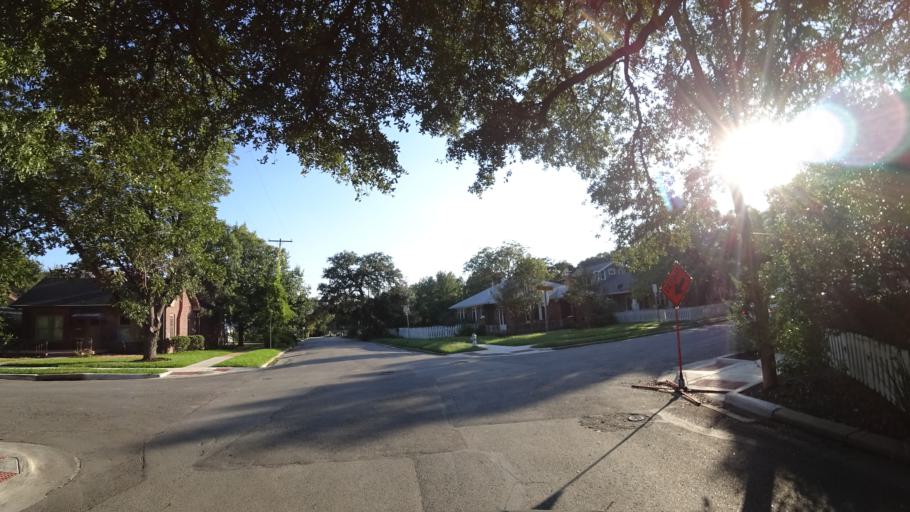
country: US
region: Texas
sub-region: Travis County
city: Austin
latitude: 30.2867
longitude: -97.7510
